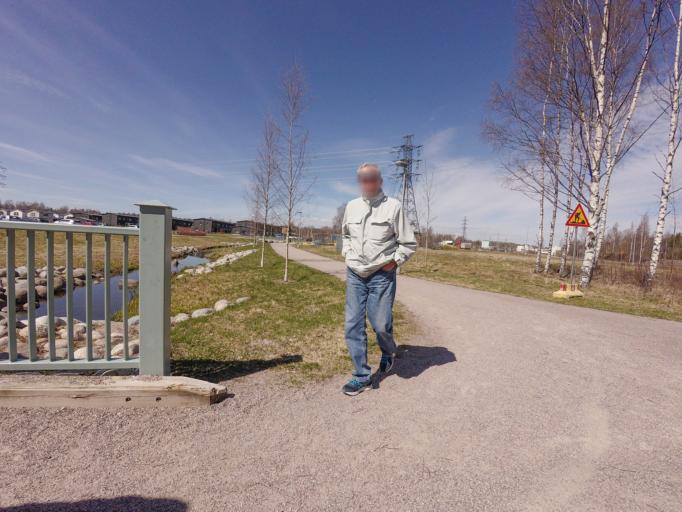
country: FI
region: Uusimaa
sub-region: Helsinki
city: Vantaa
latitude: 60.2315
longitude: 25.1128
